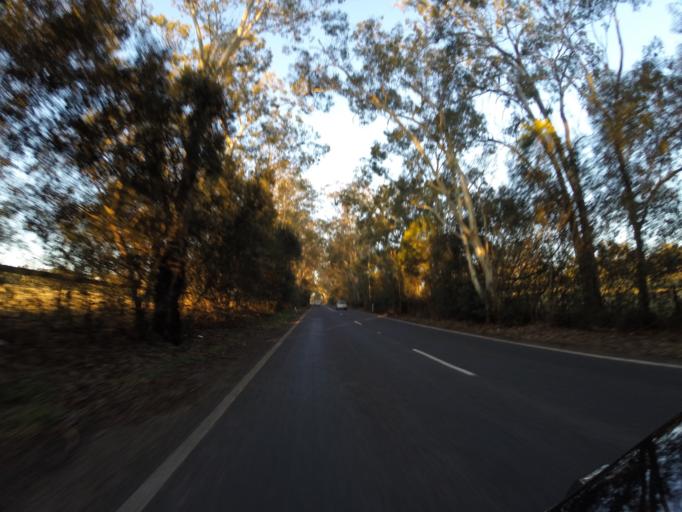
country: AU
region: New South Wales
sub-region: Camden
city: Cobbitty
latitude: -34.0159
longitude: 150.6977
